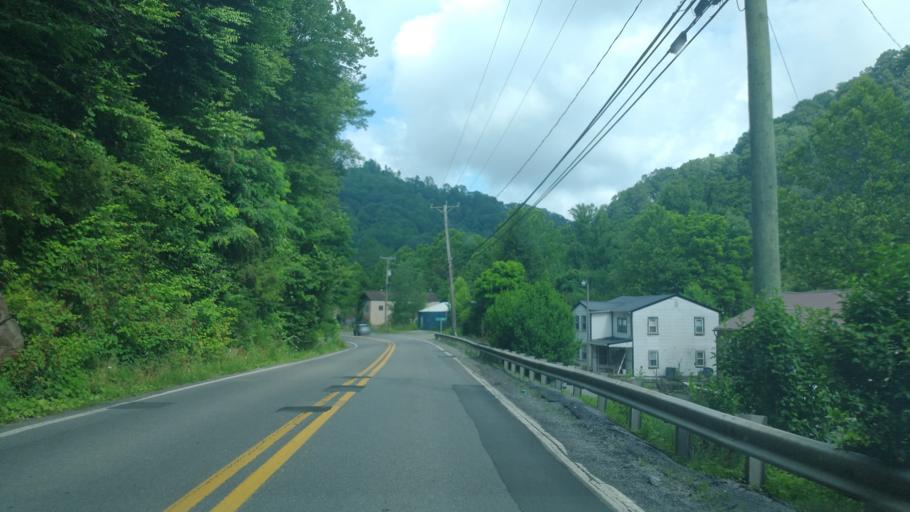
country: US
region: West Virginia
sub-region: McDowell County
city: Welch
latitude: 37.4046
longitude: -81.4210
